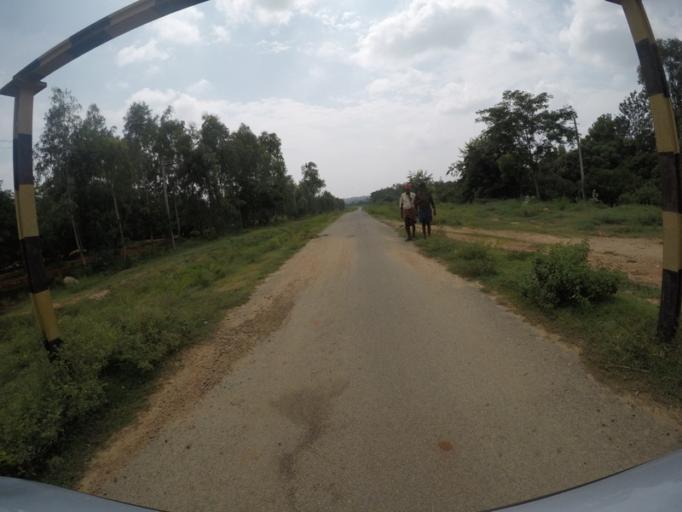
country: IN
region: Karnataka
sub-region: Ramanagara
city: Kanakapura
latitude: 12.4709
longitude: 77.3450
